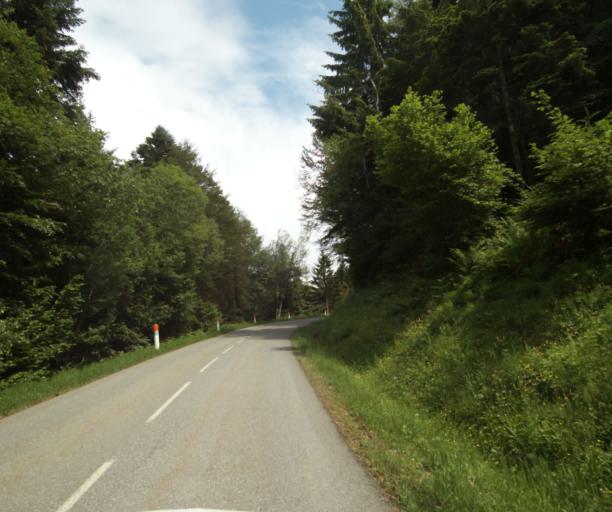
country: FR
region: Rhone-Alpes
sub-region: Departement de la Haute-Savoie
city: Perrignier
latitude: 46.2669
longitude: 6.4423
